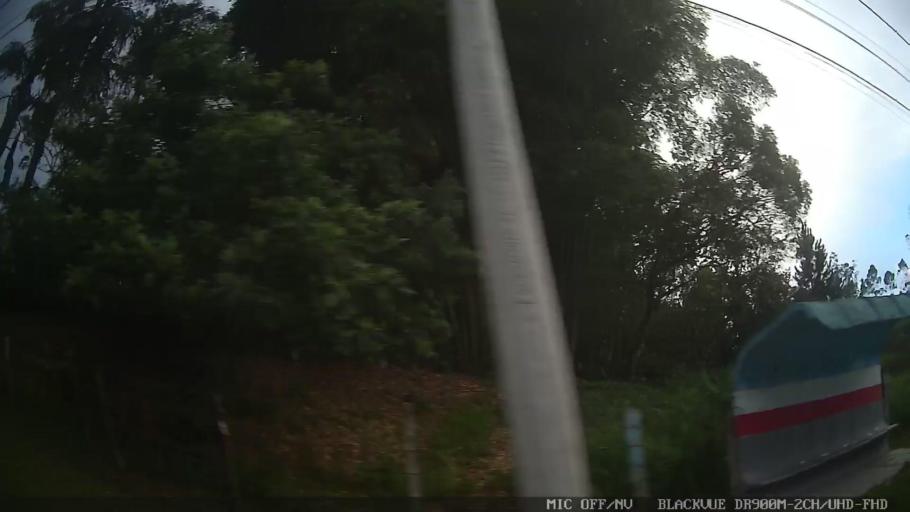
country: BR
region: Sao Paulo
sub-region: Ribeirao Pires
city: Ribeirao Pires
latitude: -23.6687
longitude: -46.3172
